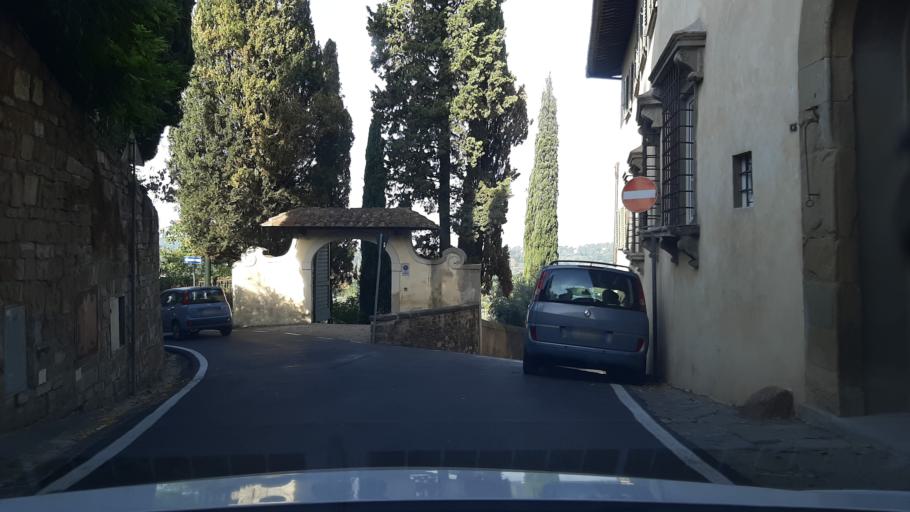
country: IT
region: Tuscany
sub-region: Province of Florence
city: Florence
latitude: 43.7522
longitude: 11.2541
